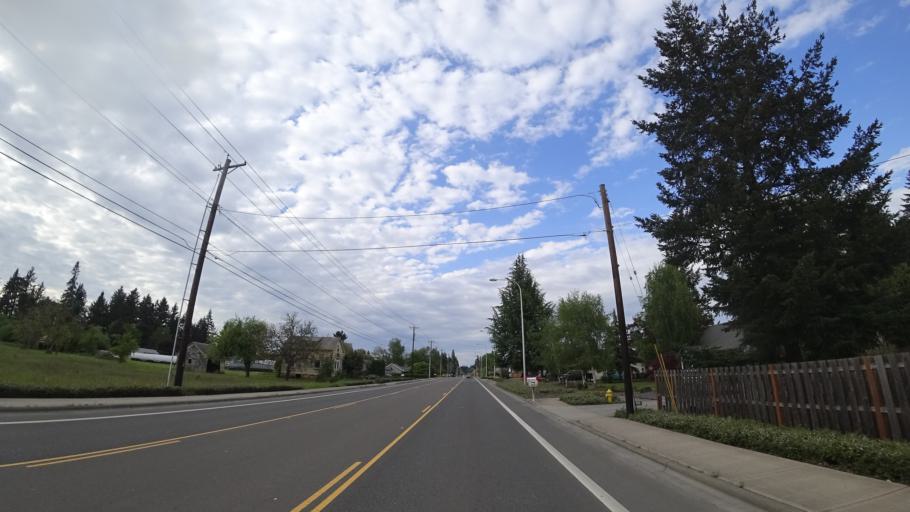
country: US
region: Oregon
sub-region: Washington County
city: Hillsboro
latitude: 45.5133
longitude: -122.9366
